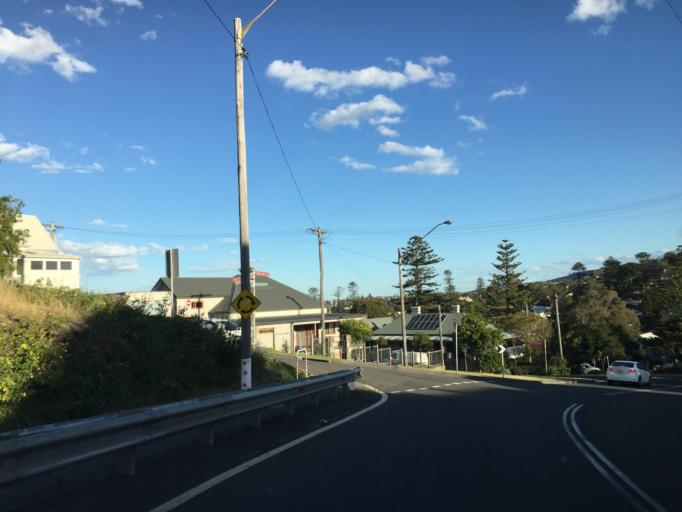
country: AU
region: New South Wales
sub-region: Kiama
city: Kiama
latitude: -34.6668
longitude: 150.8547
